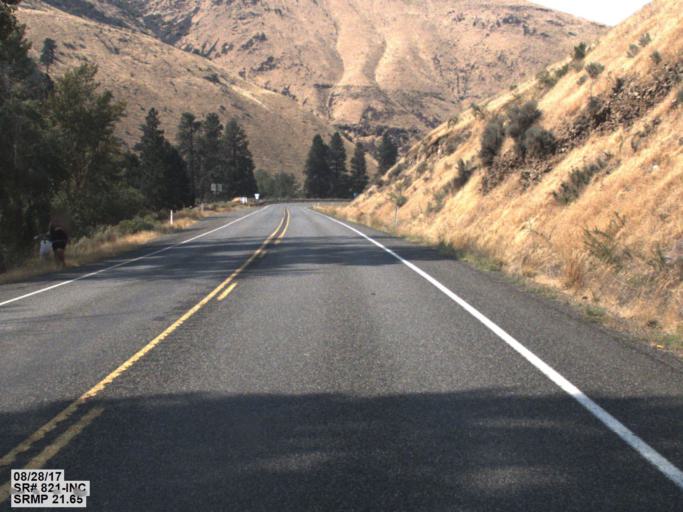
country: US
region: Washington
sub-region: Kittitas County
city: Ellensburg
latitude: 46.8945
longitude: -120.5003
